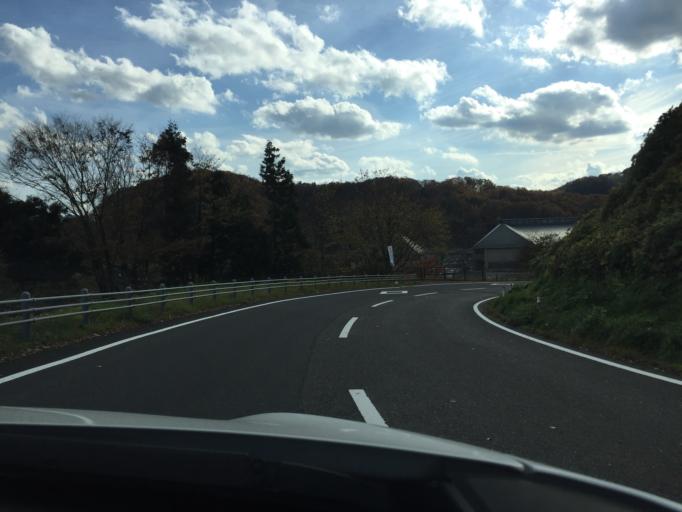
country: JP
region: Fukushima
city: Miharu
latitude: 37.4070
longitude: 140.4755
